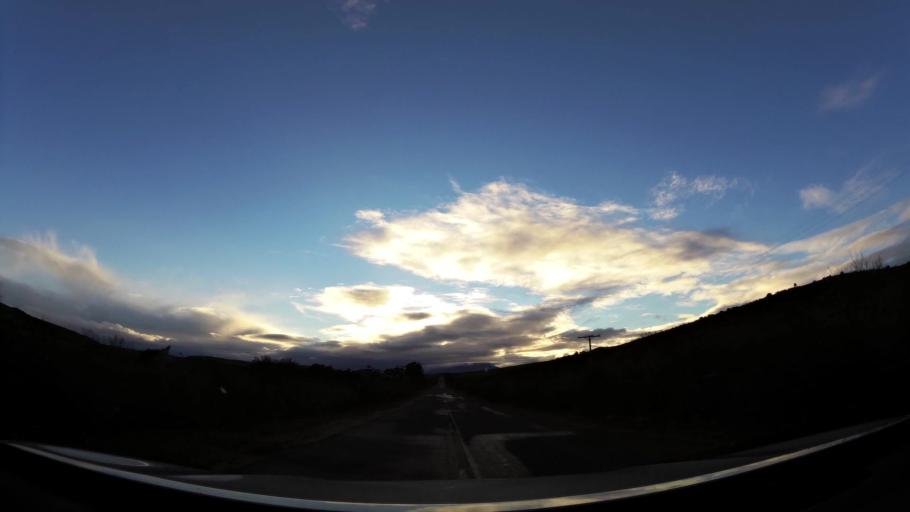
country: ZA
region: Western Cape
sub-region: Eden District Municipality
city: Riversdale
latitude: -34.0664
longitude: 20.8948
